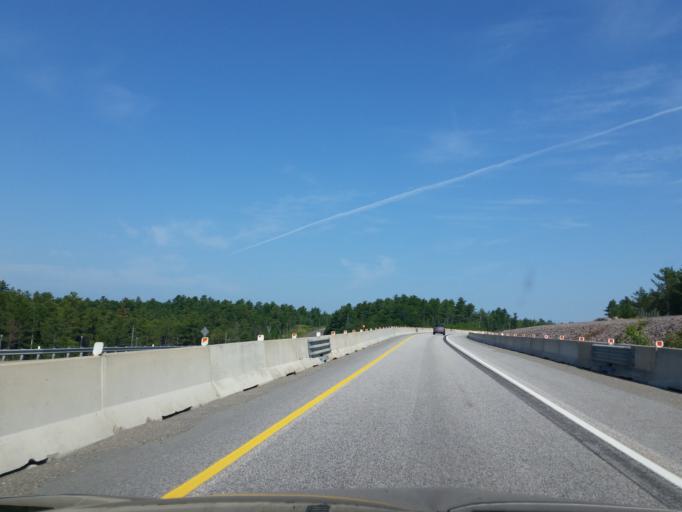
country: CA
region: Ontario
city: Greater Sudbury
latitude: 46.2038
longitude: -80.7617
